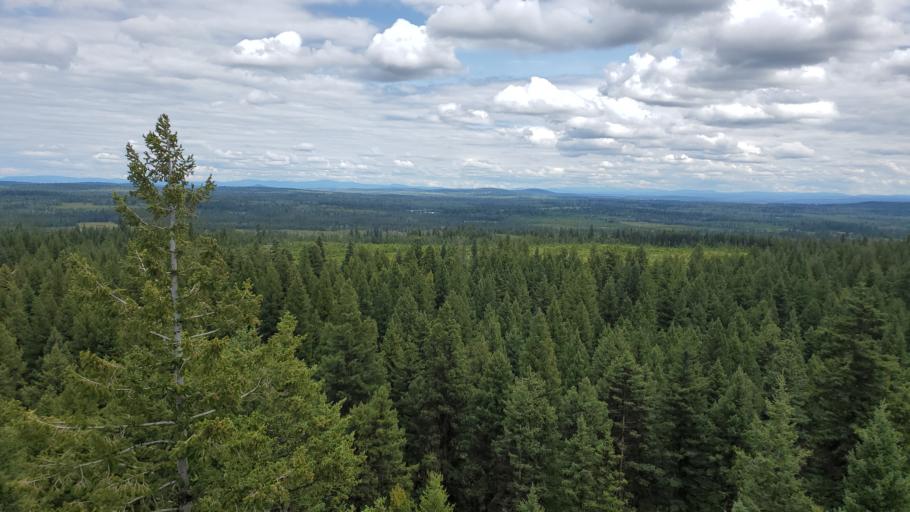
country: CA
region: British Columbia
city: Cache Creek
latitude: 51.4759
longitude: -121.3667
